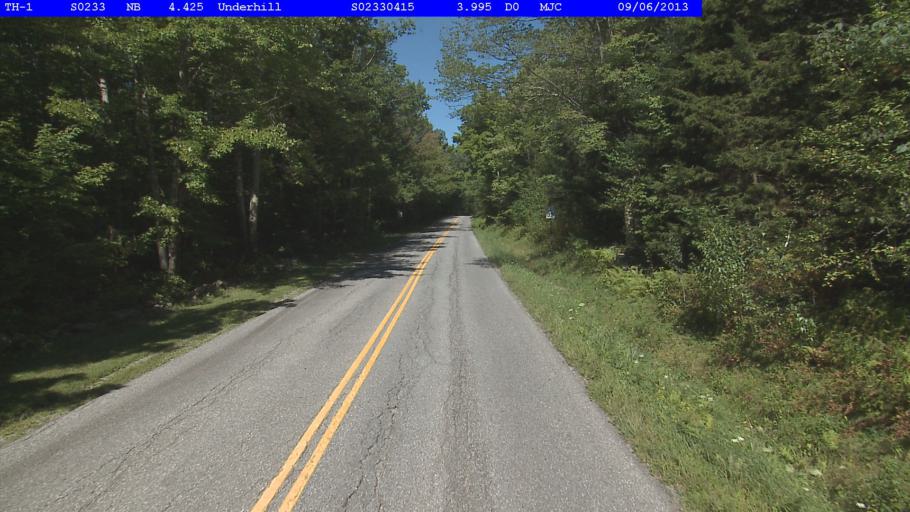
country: US
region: Vermont
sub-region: Chittenden County
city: Jericho
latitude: 44.5245
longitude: -72.8800
